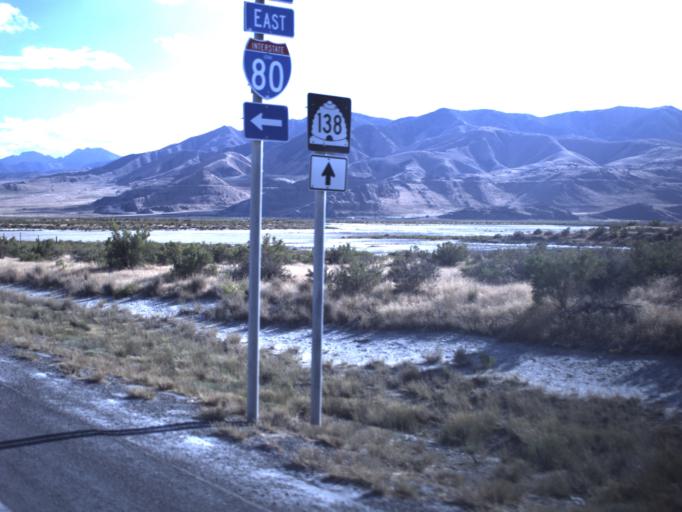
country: US
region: Utah
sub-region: Tooele County
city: Grantsville
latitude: 40.7053
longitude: -112.5301
